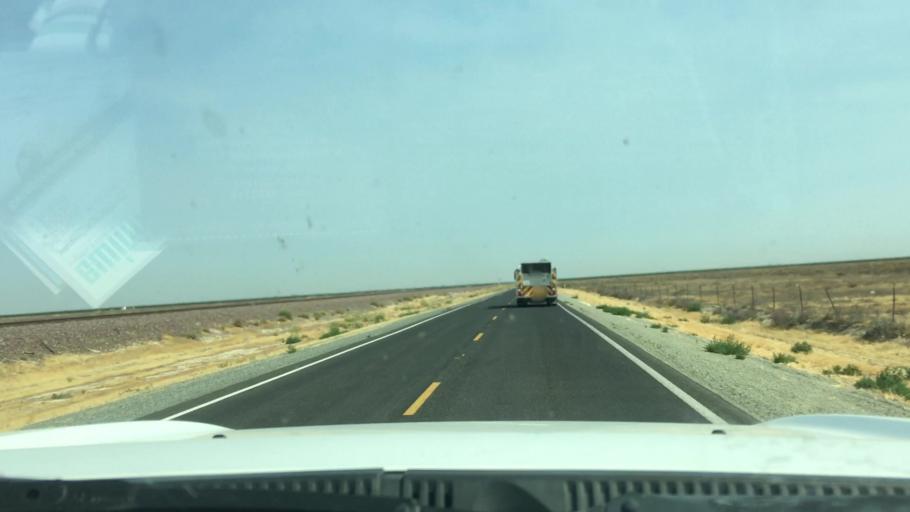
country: US
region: California
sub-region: Kern County
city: Delano
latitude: 35.7954
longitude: -119.3569
